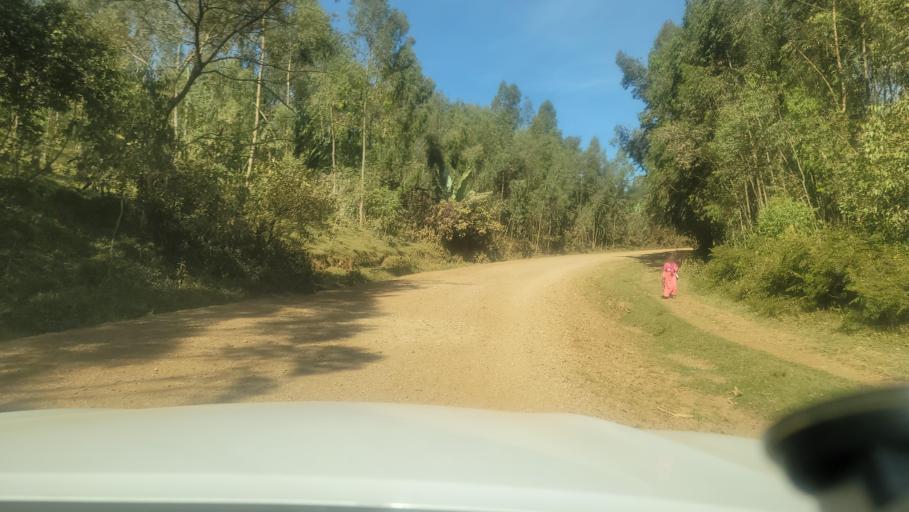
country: ET
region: Oromiya
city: Agaro
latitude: 7.8003
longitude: 36.4668
